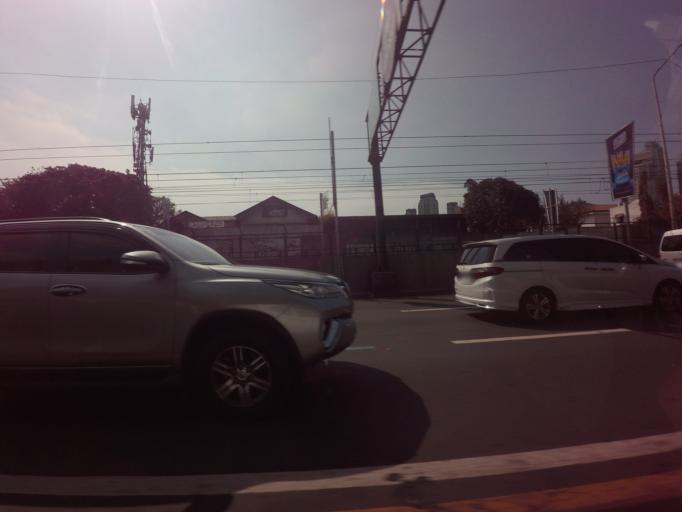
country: PH
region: Metro Manila
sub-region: Makati City
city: Makati City
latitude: 14.5445
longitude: 121.0231
